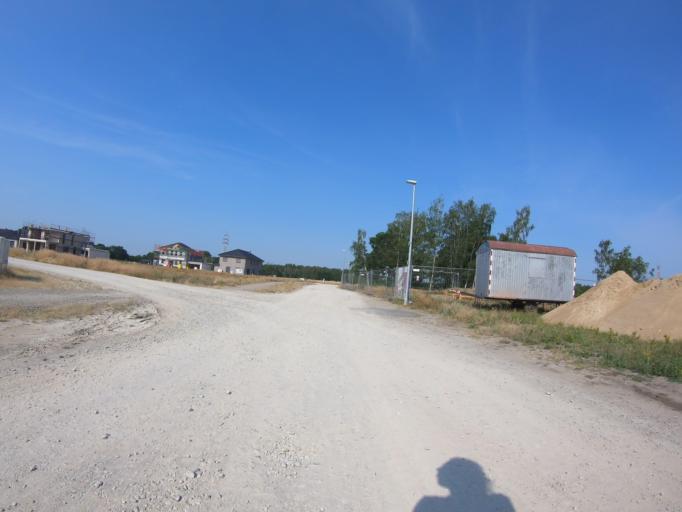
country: DE
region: Lower Saxony
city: Gifhorn
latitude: 52.4906
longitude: 10.5320
